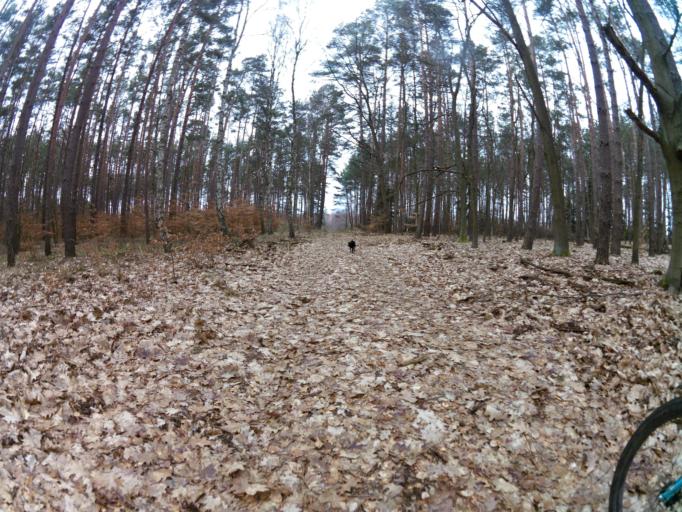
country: PL
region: Lubusz
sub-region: Powiat gorzowski
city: Witnica
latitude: 52.7700
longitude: 14.8276
